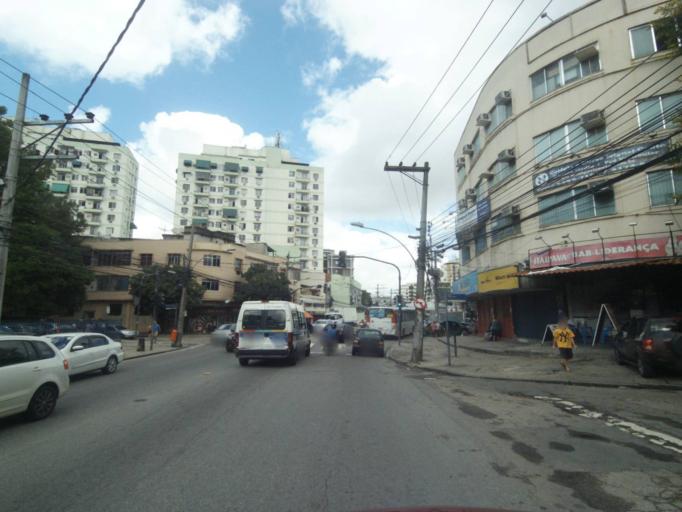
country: BR
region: Rio de Janeiro
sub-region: Sao Joao De Meriti
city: Sao Joao de Meriti
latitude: -22.9199
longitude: -43.3604
